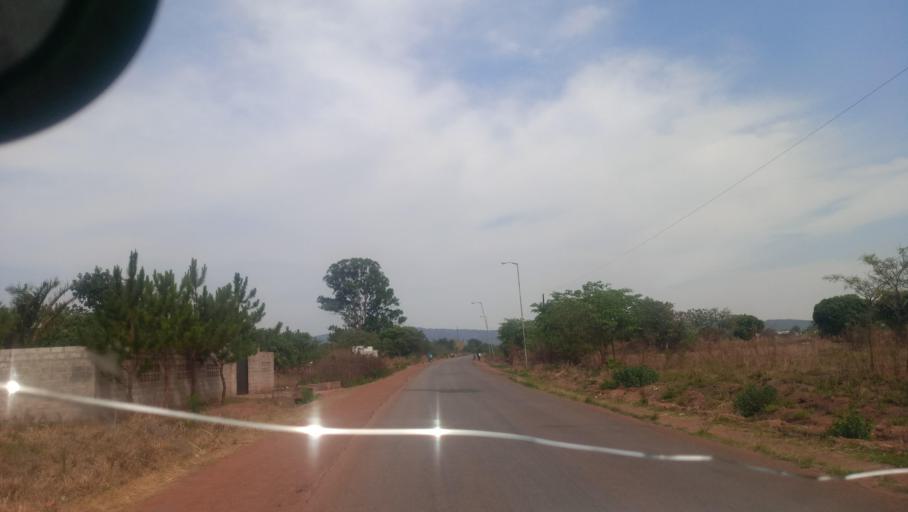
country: ZM
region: Northern
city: Mpika
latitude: -11.8335
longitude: 31.4234
